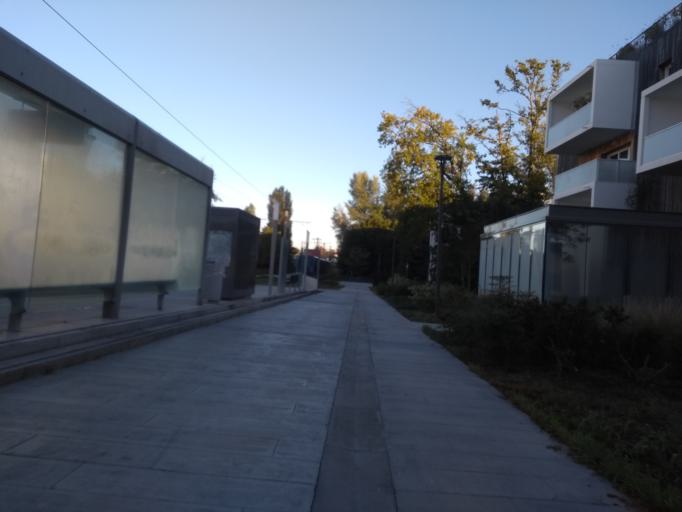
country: FR
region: Aquitaine
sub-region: Departement de la Gironde
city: Pessac
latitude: 44.8003
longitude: -0.6346
